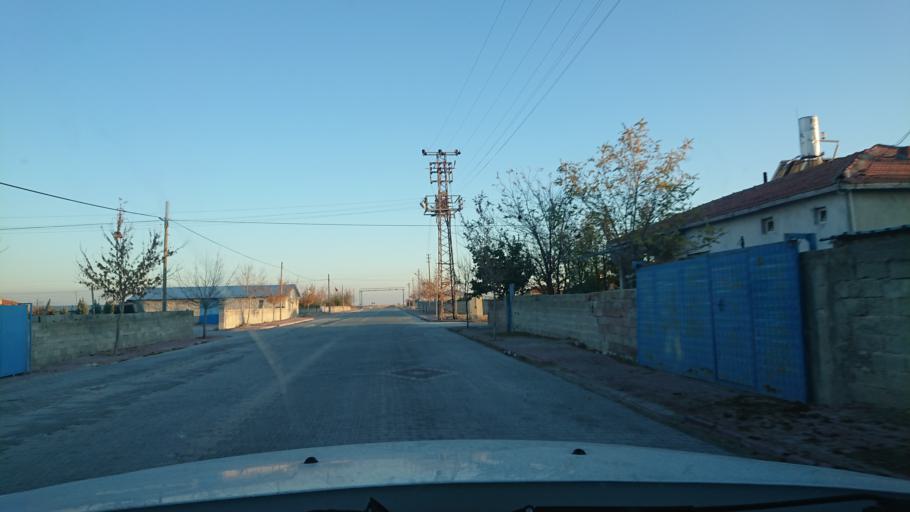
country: TR
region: Aksaray
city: Eskil
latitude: 38.3947
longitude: 33.4247
